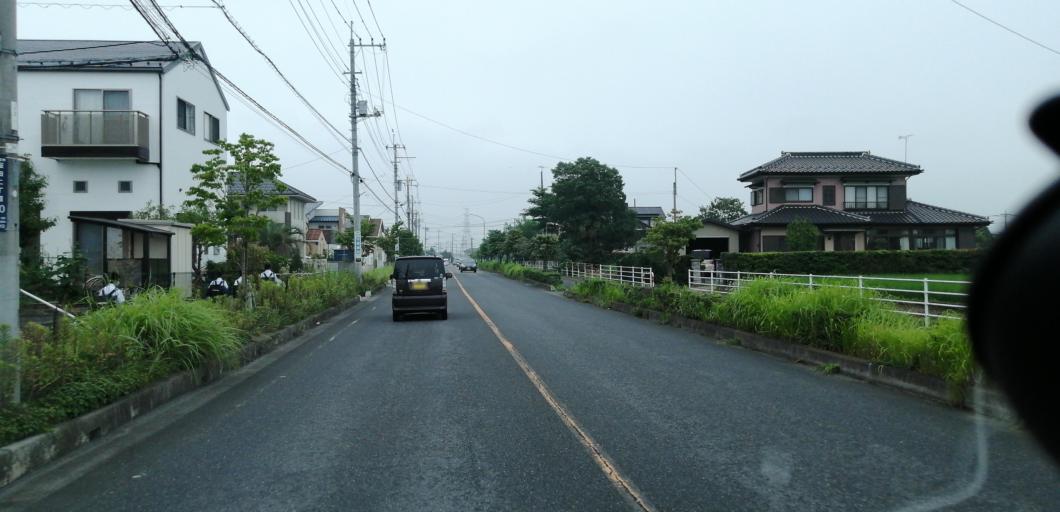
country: JP
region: Saitama
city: Kukichuo
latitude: 36.0971
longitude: 139.6843
